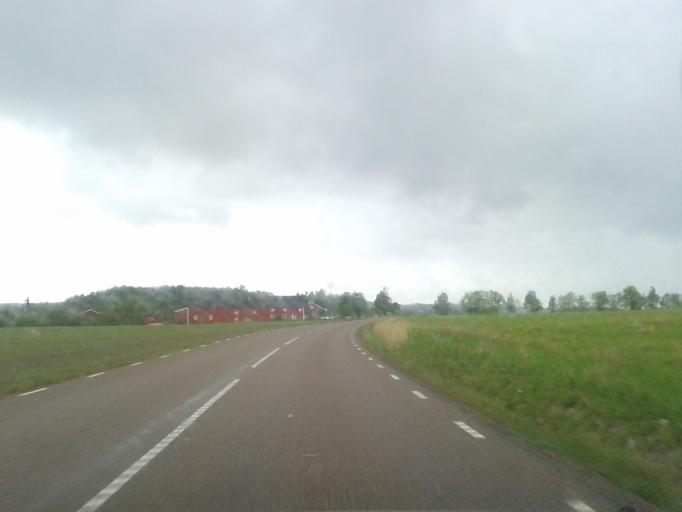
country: SE
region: Vaestra Goetaland
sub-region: Lilla Edets Kommun
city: Lilla Edet
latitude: 58.1187
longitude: 12.1150
